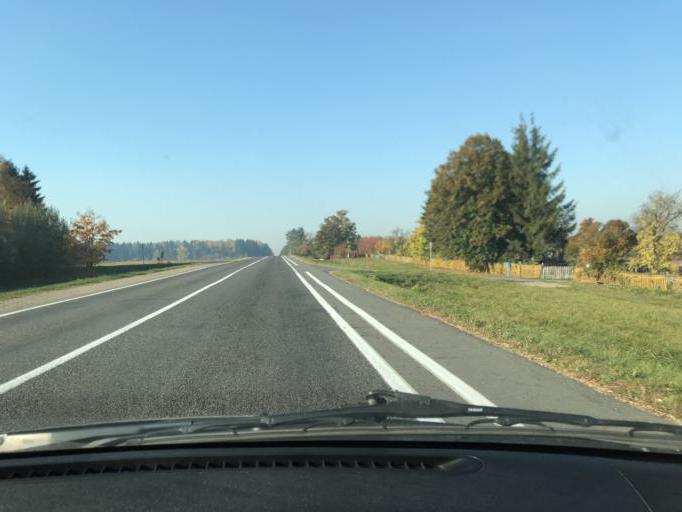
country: BY
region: Minsk
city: Klyetsk
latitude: 52.9704
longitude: 26.6511
